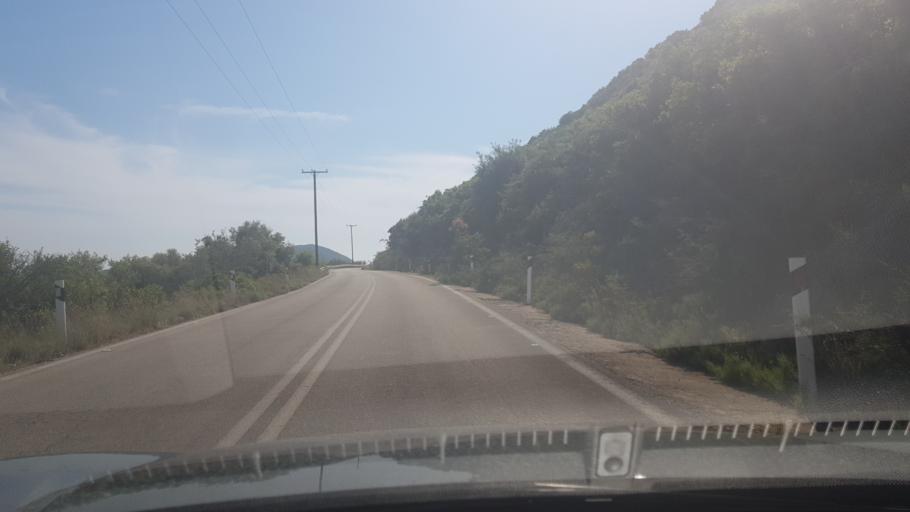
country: GR
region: Ionian Islands
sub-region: Lefkada
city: Nidri
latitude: 38.6510
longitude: 20.6644
